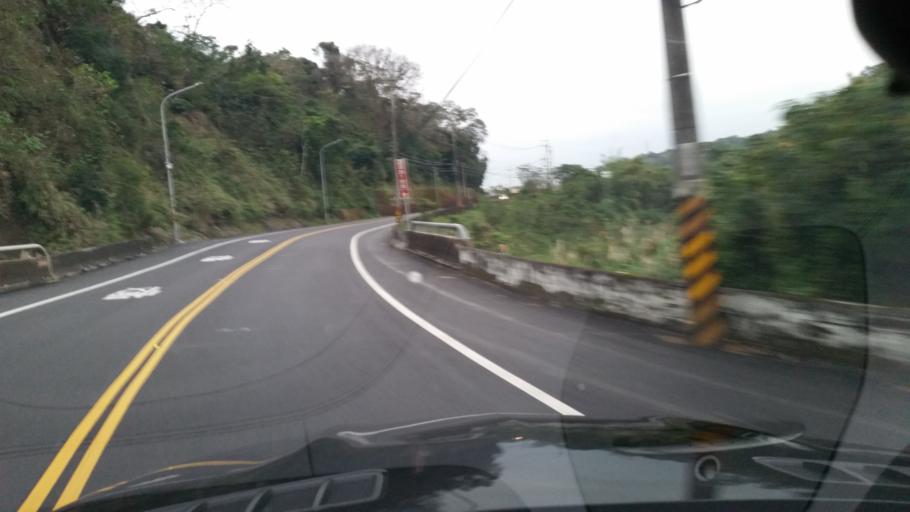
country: TW
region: Taiwan
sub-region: Miaoli
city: Miaoli
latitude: 24.5823
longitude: 120.8774
